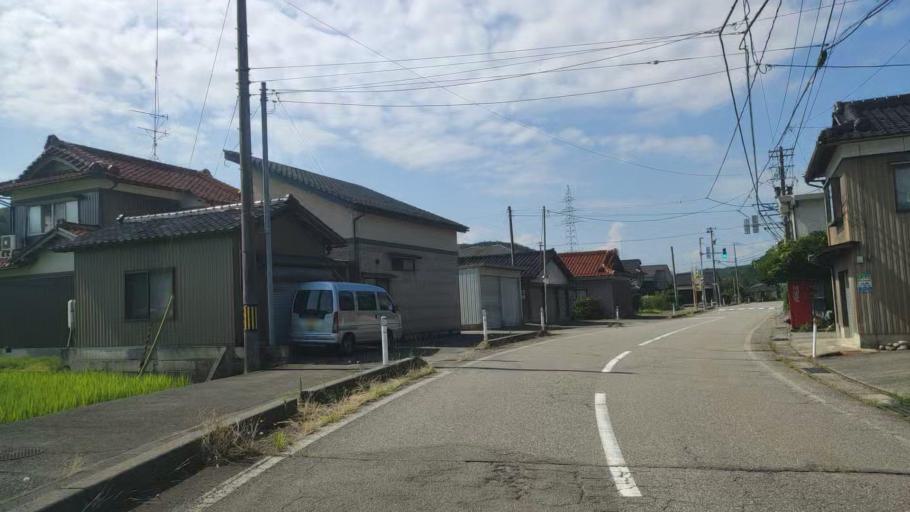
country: JP
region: Ishikawa
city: Komatsu
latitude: 36.3710
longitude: 136.4979
